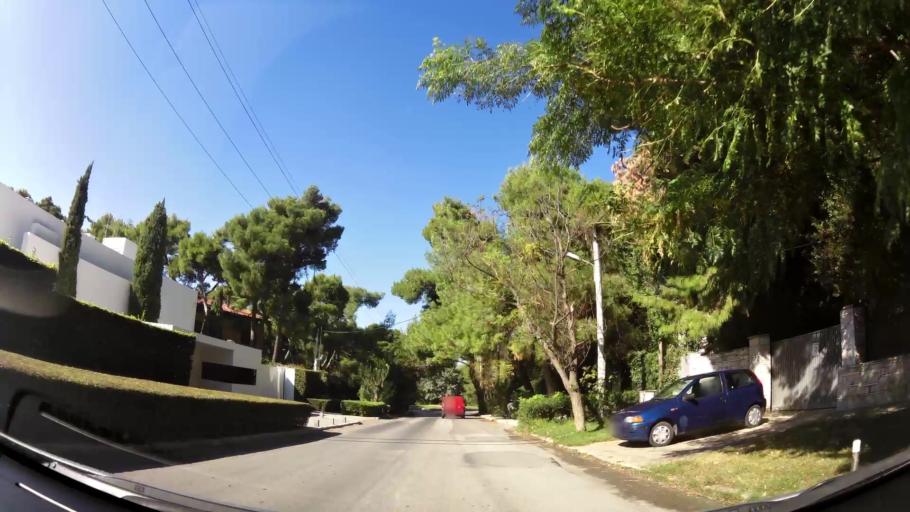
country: GR
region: Attica
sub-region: Nomarchia Athinas
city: Ekali
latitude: 38.1129
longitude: 23.8394
